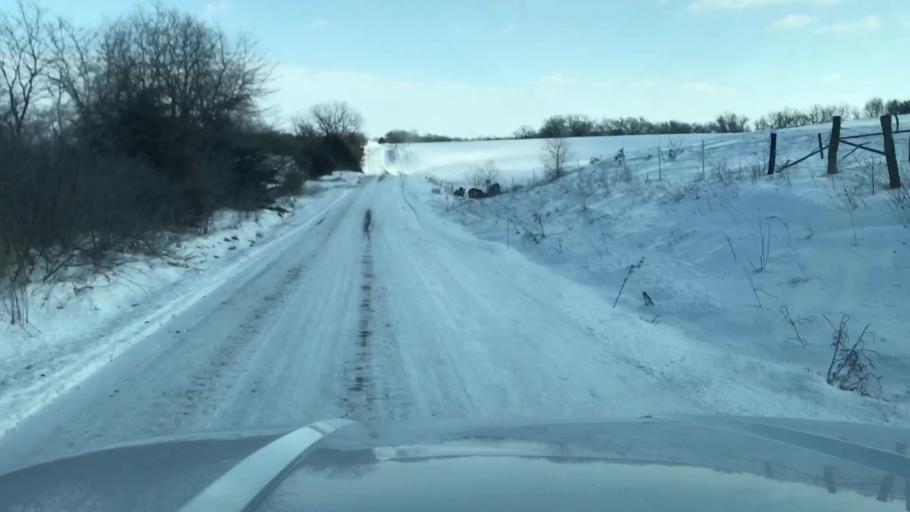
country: US
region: Missouri
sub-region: Nodaway County
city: Maryville
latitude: 40.3867
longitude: -94.7077
